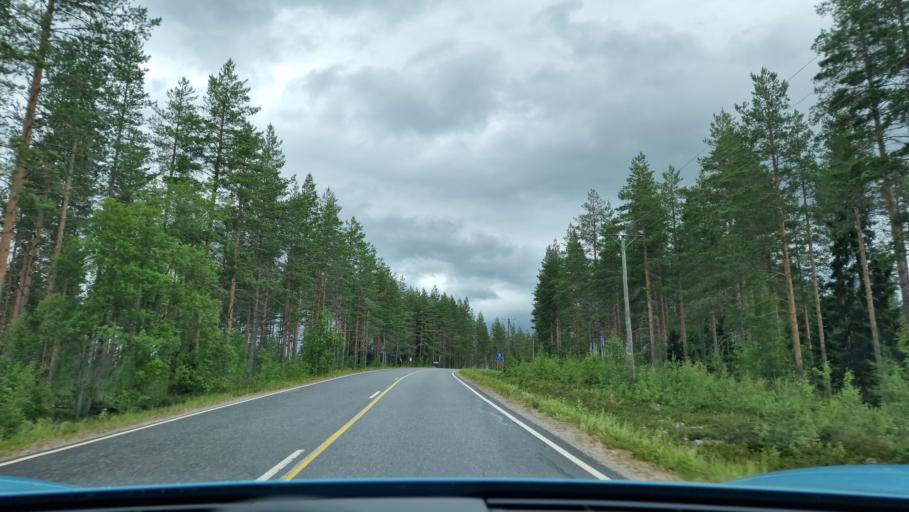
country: FI
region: Southern Ostrobothnia
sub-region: Jaerviseutu
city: Soini
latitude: 62.7420
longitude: 24.4126
